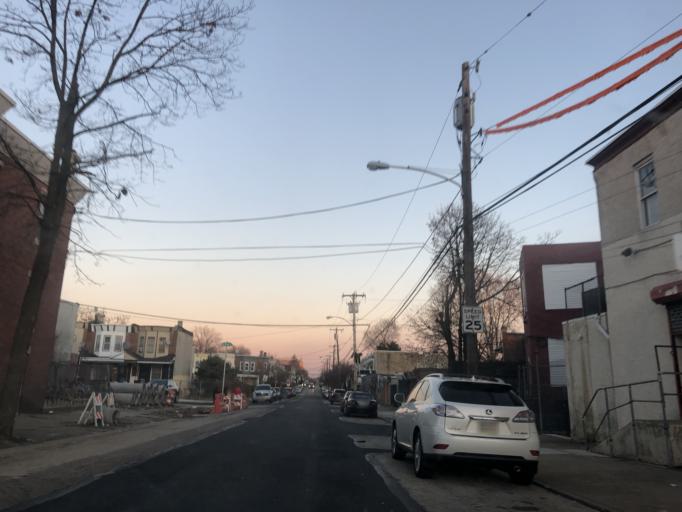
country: US
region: Pennsylvania
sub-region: Delaware County
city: Millbourne
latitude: 39.9722
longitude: -75.2448
